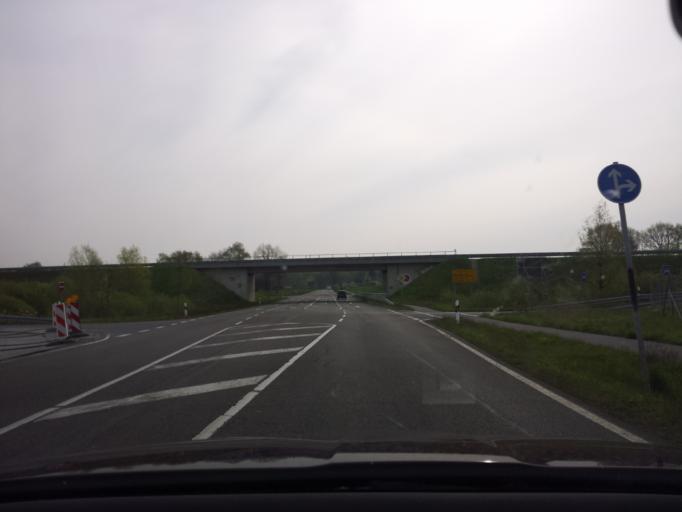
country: DE
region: Brandenburg
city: Luckau
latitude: 51.8535
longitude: 13.6849
